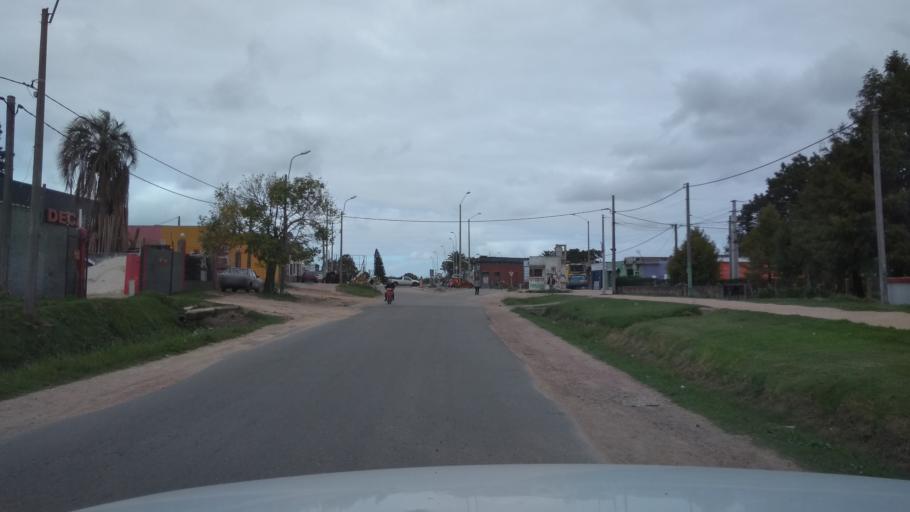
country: UY
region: Canelones
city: Toledo
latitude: -34.7801
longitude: -56.1367
